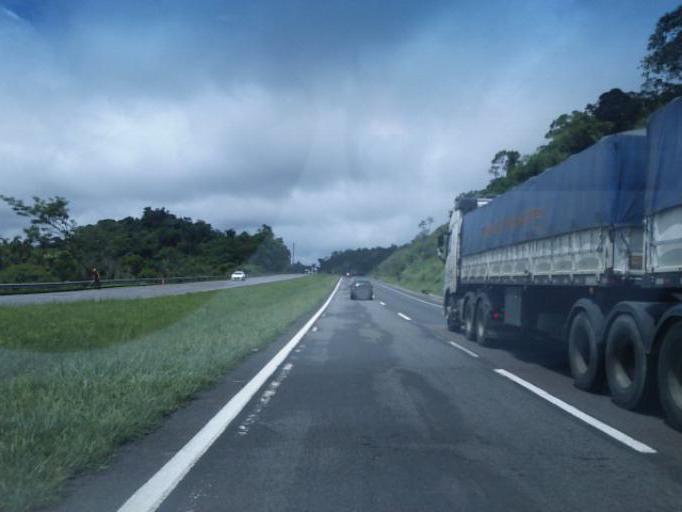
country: BR
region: Parana
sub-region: Antonina
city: Antonina
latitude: -25.0923
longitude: -48.6487
